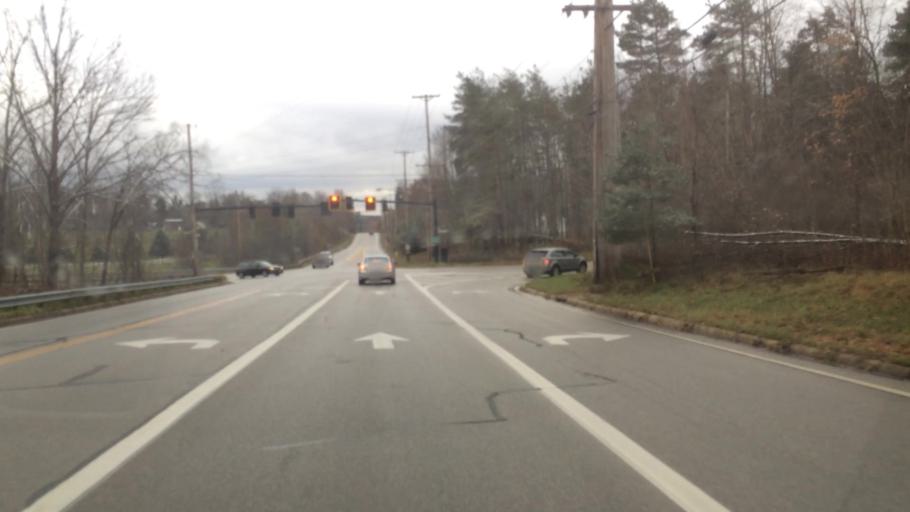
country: US
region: Ohio
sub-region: Summit County
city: Hudson
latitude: 41.2101
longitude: -81.4114
